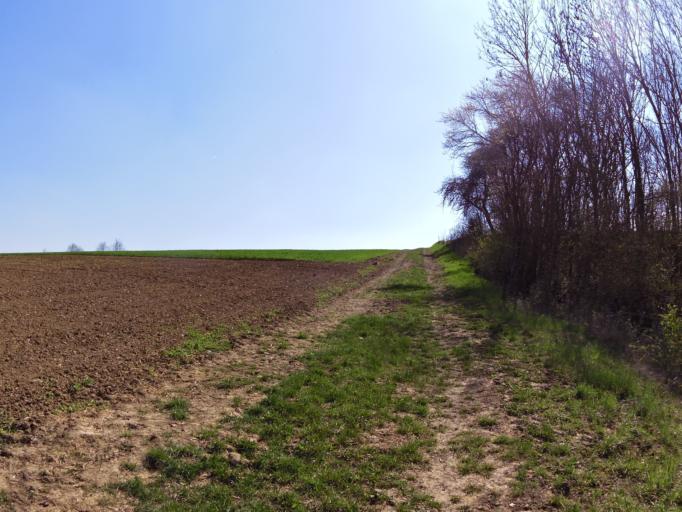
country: DE
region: Bavaria
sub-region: Regierungsbezirk Unterfranken
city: Biebelried
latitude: 49.7852
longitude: 10.0732
